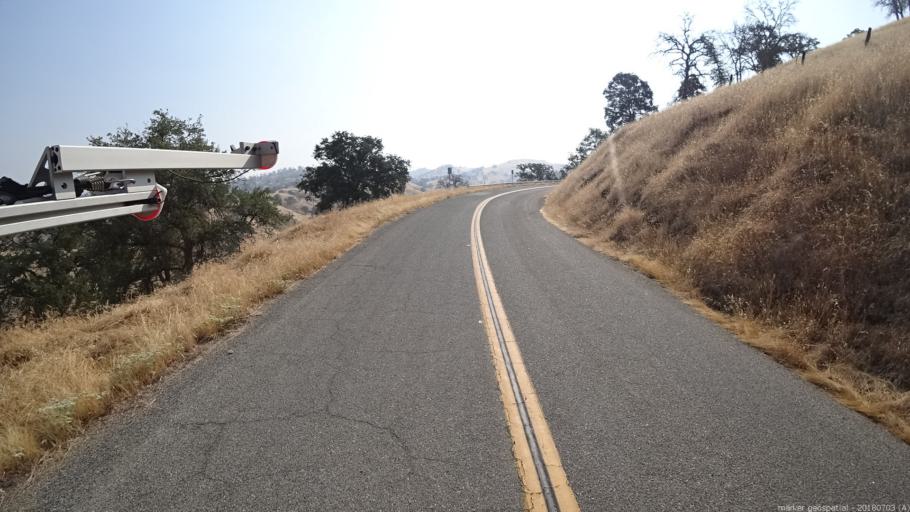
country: US
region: California
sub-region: Madera County
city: Yosemite Lakes
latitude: 37.0301
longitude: -119.7049
